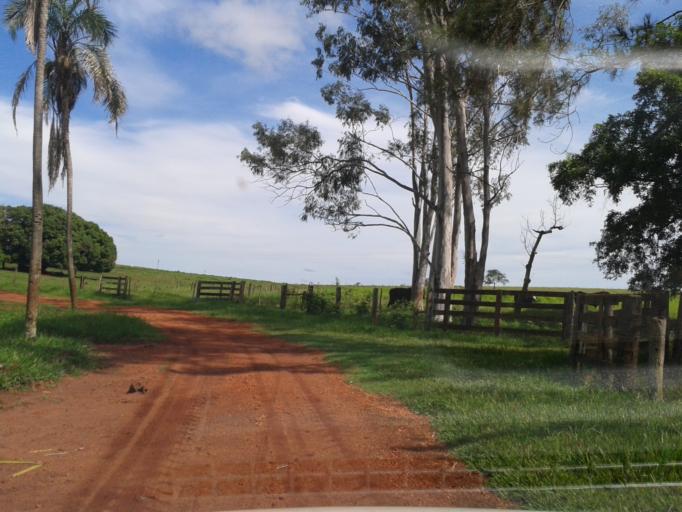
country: BR
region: Minas Gerais
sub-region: Santa Vitoria
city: Santa Vitoria
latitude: -19.2060
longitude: -50.6830
